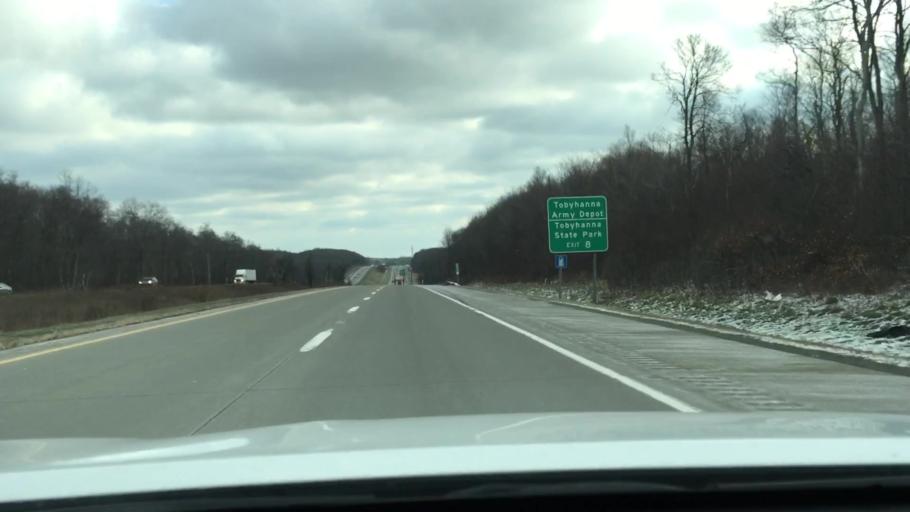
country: US
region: Pennsylvania
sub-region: Monroe County
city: Pocono Pines
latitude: 41.1959
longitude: -75.4501
